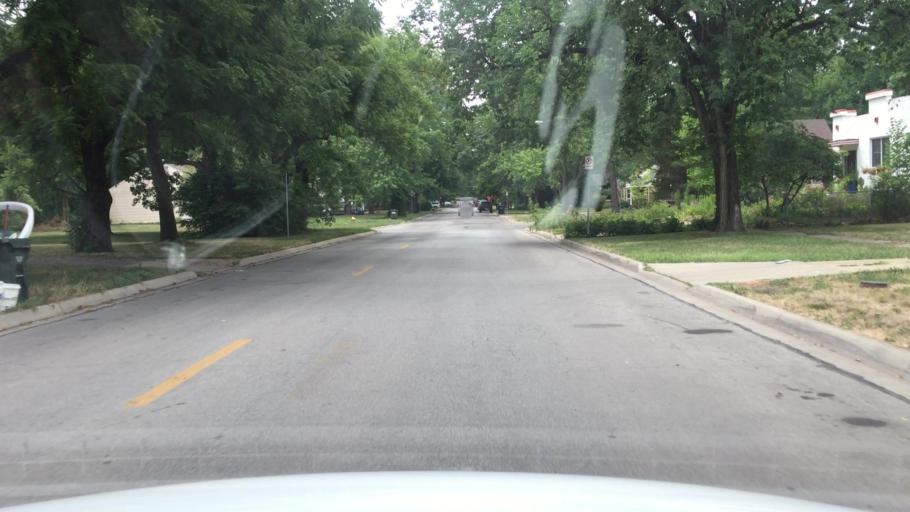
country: US
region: Kansas
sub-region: Douglas County
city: Lawrence
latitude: 38.9488
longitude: -95.2395
